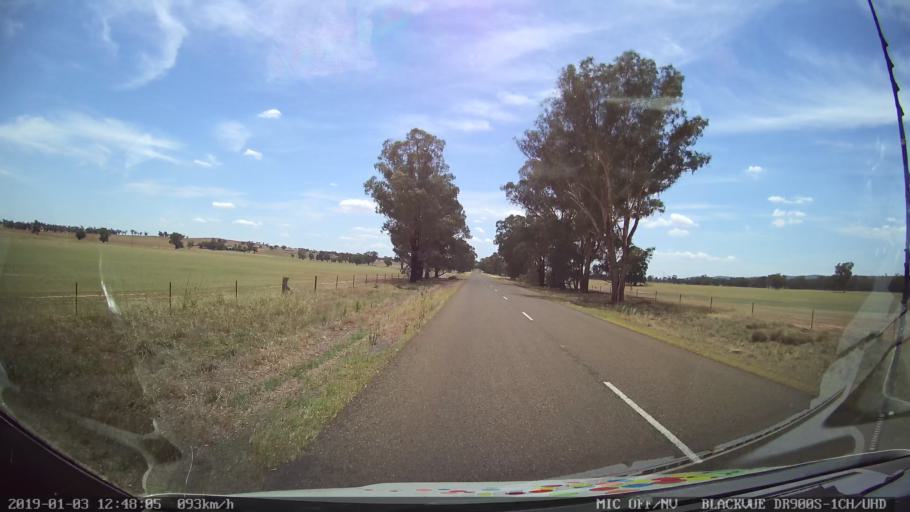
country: AU
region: New South Wales
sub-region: Weddin
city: Grenfell
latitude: -33.7187
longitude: 148.2475
